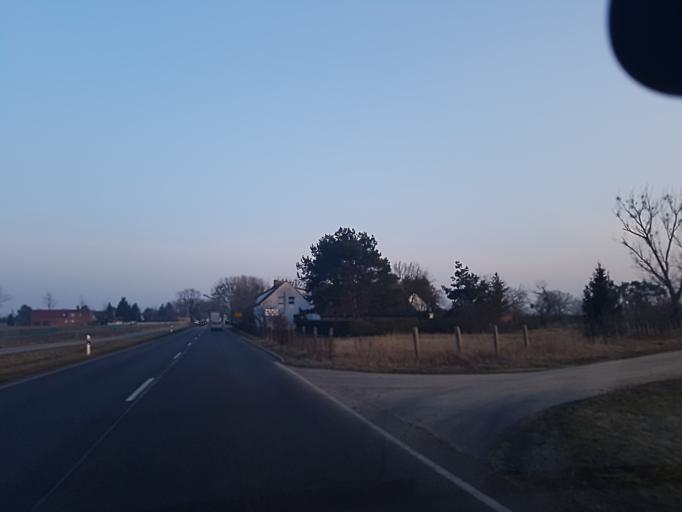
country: DE
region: Saxony-Anhalt
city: Muhlanger
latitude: 51.8397
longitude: 12.7812
